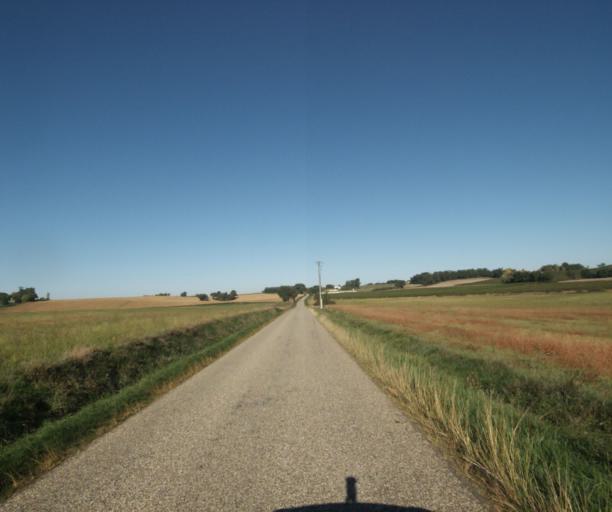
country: FR
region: Midi-Pyrenees
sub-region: Departement du Gers
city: Gondrin
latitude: 43.8262
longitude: 0.2677
